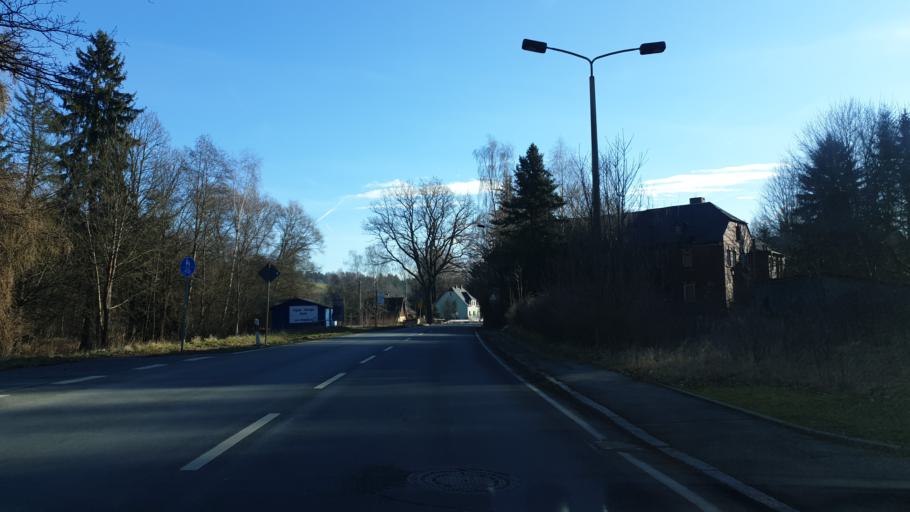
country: DE
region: Saxony
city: Adorf
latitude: 50.2961
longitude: 12.2599
